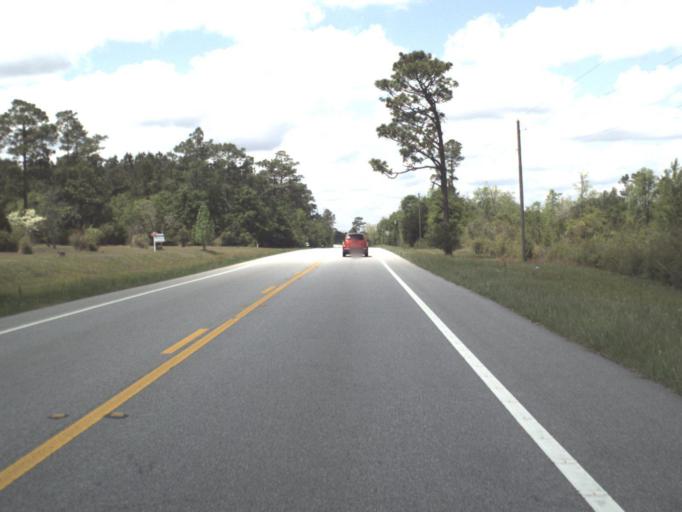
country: US
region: Florida
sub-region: Escambia County
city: Molino
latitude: 30.7838
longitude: -87.4055
